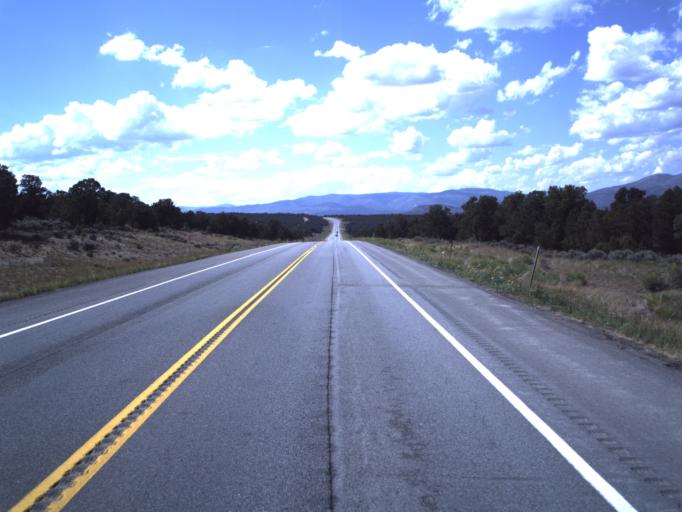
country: US
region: Utah
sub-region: Duchesne County
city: Duchesne
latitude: 40.1873
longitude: -110.6720
